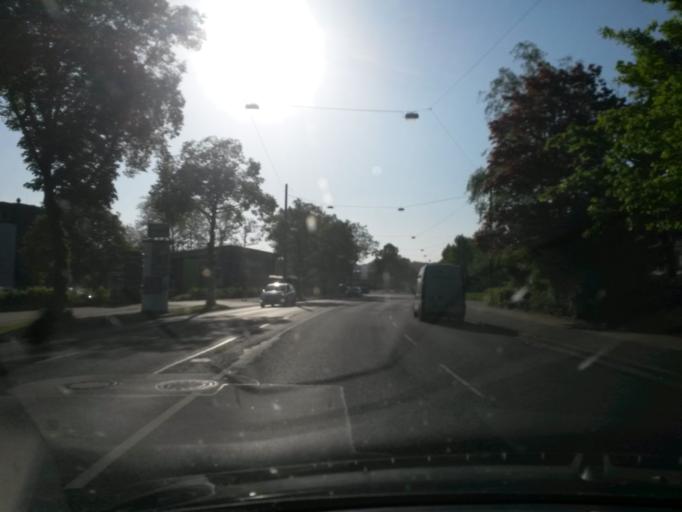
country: DE
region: North Rhine-Westphalia
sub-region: Regierungsbezirk Detmold
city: Bielefeld
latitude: 52.0121
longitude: 8.5670
